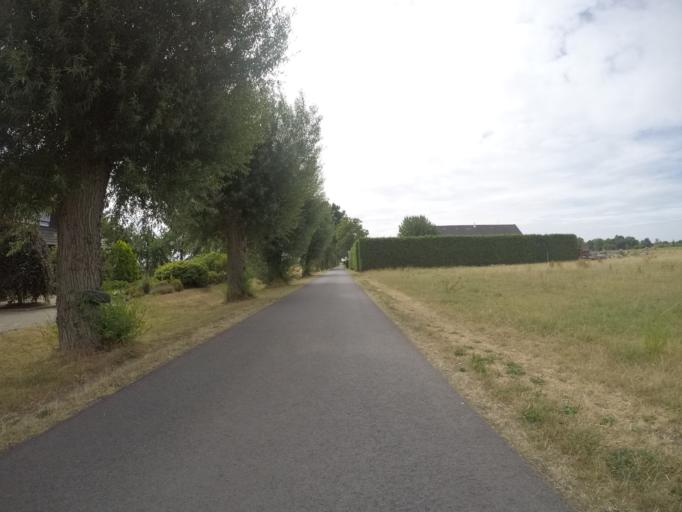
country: DE
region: North Rhine-Westphalia
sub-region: Regierungsbezirk Dusseldorf
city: Bocholt
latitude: 51.8511
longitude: 6.5590
